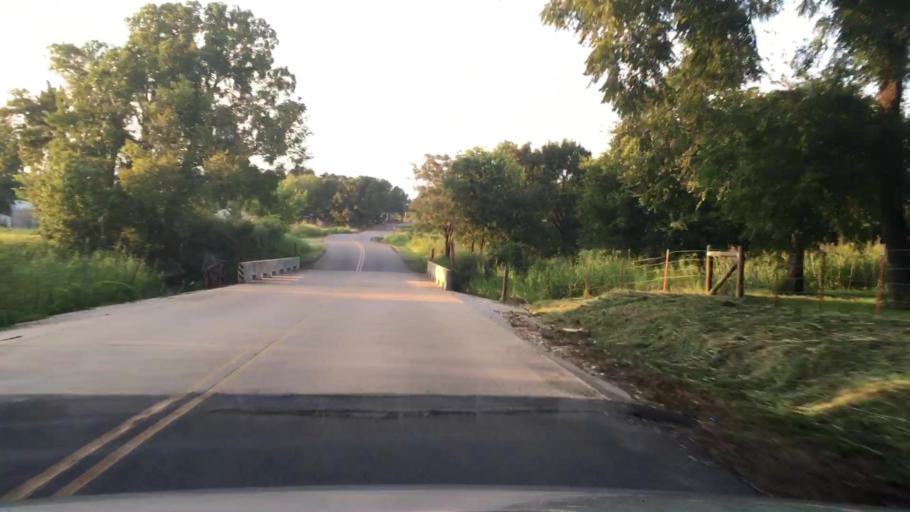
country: US
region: Oklahoma
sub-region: Muskogee County
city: Fort Gibson
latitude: 35.8992
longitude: -95.1627
